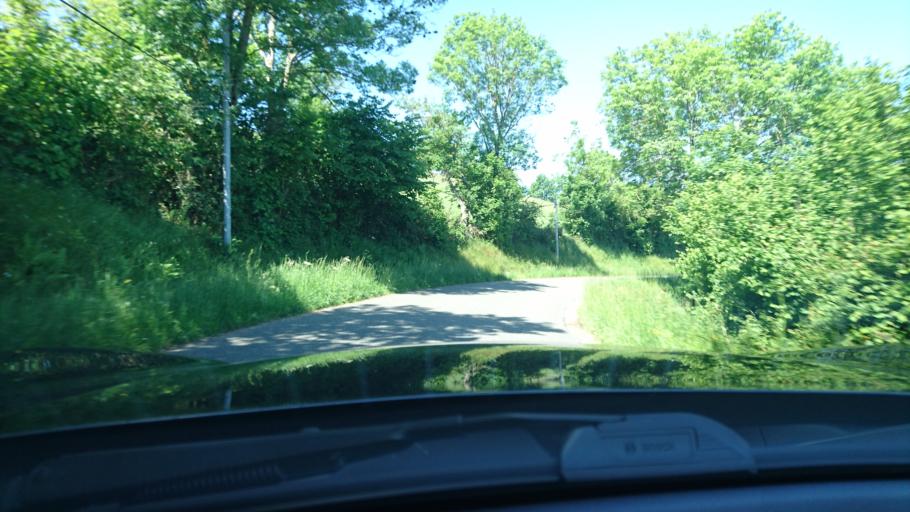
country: FR
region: Rhone-Alpes
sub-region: Departement de la Loire
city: Bussieres
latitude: 45.8770
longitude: 4.2848
